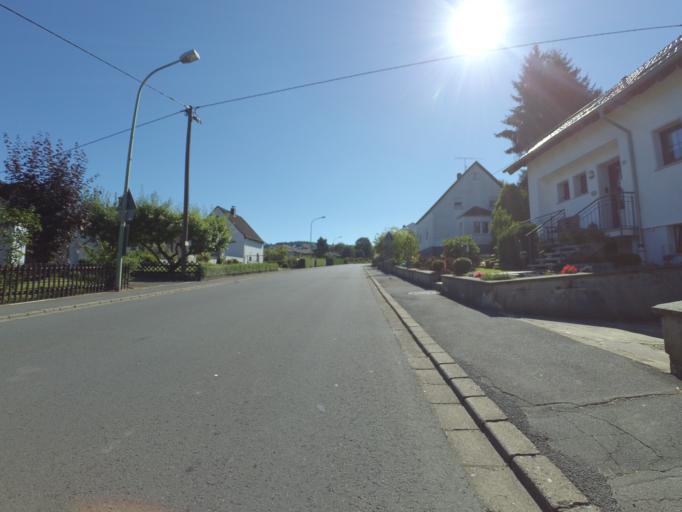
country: DE
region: Rheinland-Pfalz
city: Daun
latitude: 50.2059
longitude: 6.8409
